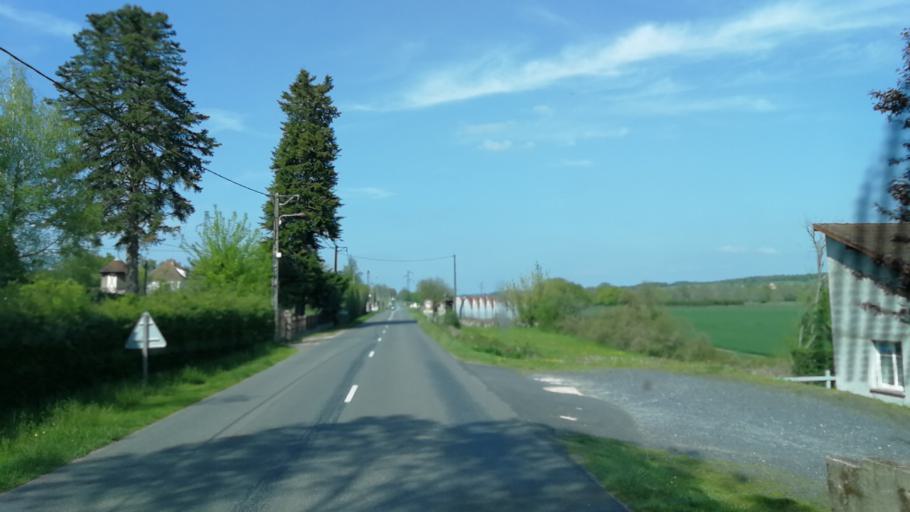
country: FR
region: Auvergne
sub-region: Departement de l'Allier
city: Saint-Gerand-le-Puy
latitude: 46.3834
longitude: 3.5838
